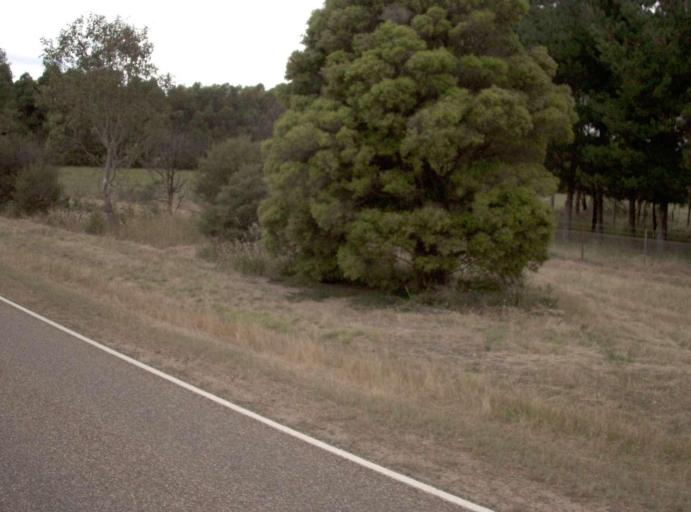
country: AU
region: Victoria
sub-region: Wellington
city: Sale
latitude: -38.0031
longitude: 147.2572
